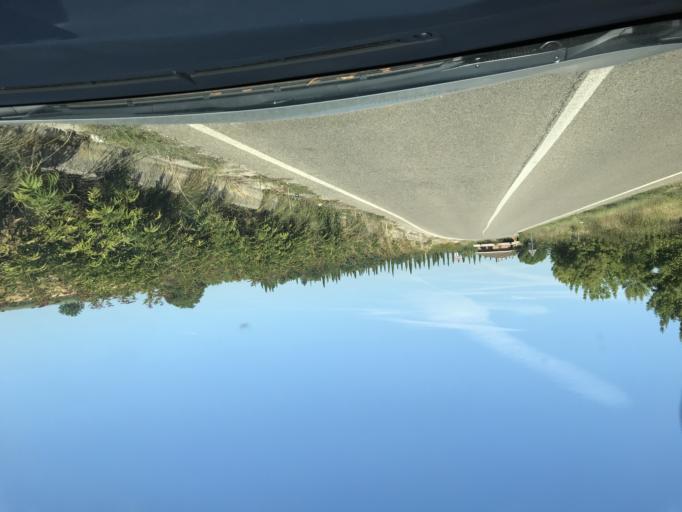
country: IT
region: Umbria
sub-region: Provincia di Perugia
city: Via Lippia
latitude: 43.1041
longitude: 12.4834
